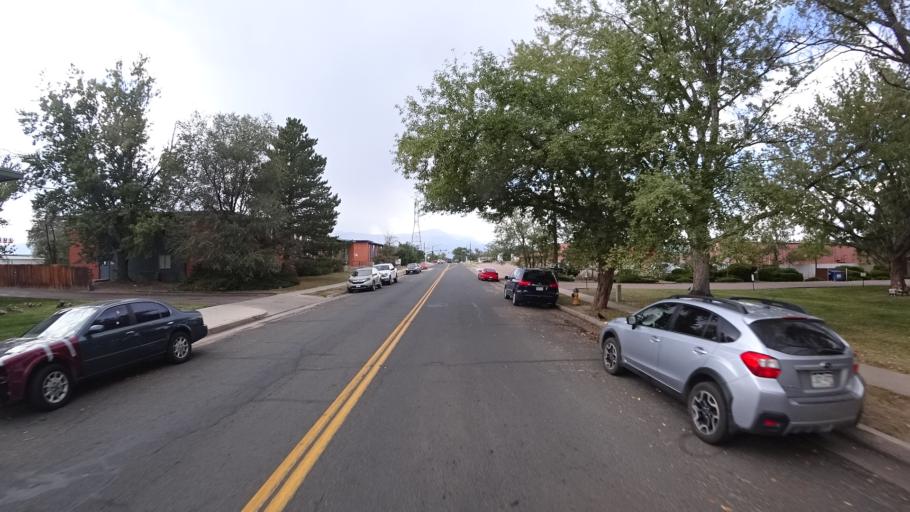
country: US
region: Colorado
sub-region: El Paso County
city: Cimarron Hills
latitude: 38.8512
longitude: -104.7550
